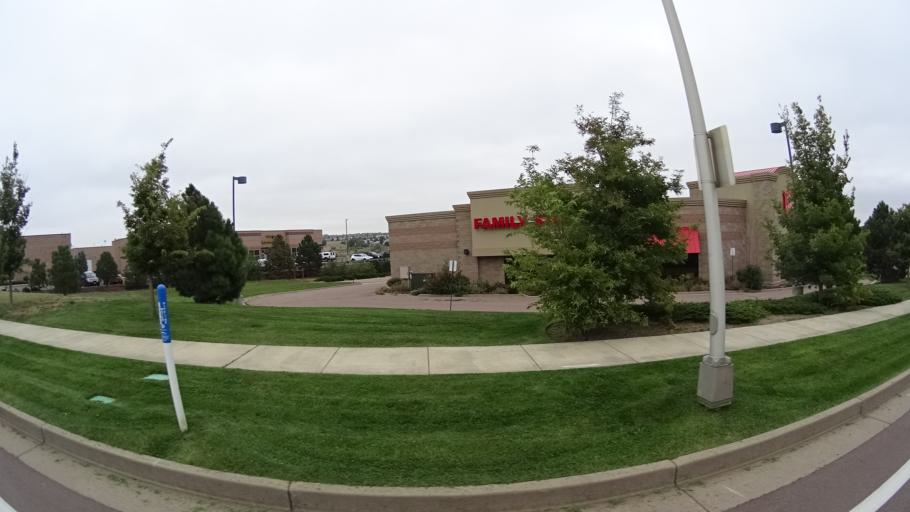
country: US
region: Colorado
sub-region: El Paso County
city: Cimarron Hills
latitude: 38.8890
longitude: -104.7144
